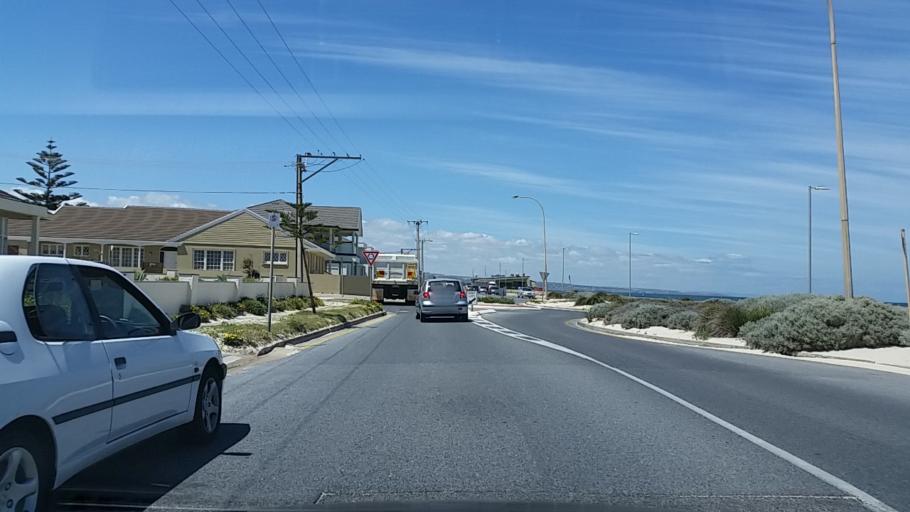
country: AU
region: South Australia
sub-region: Charles Sturt
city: Henley Beach
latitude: -34.9438
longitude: 138.5009
